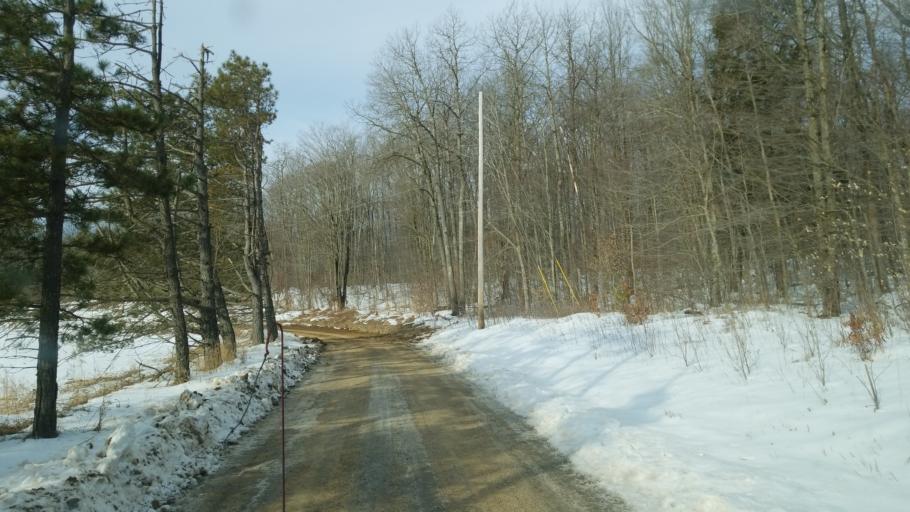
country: US
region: Pennsylvania
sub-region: Tioga County
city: Westfield
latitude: 41.9595
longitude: -77.7257
